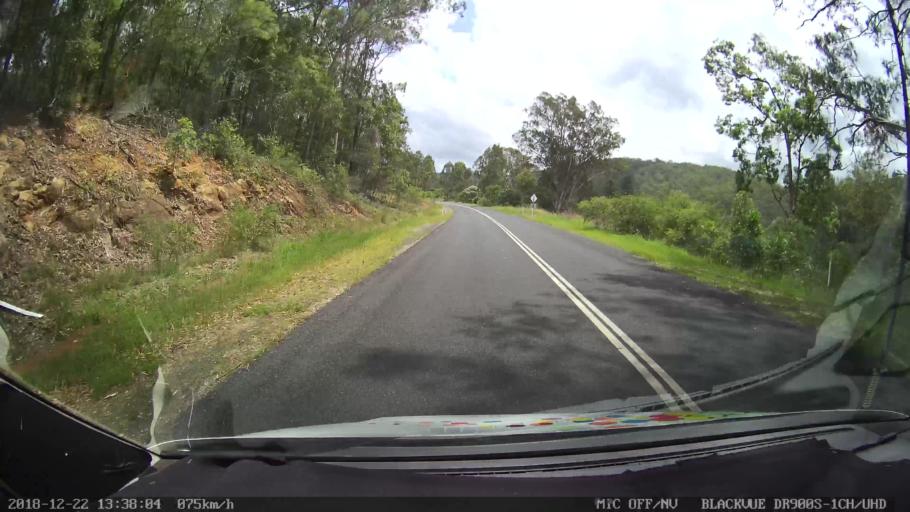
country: AU
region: New South Wales
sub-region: Clarence Valley
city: Coutts Crossing
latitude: -29.8961
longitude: 152.7890
